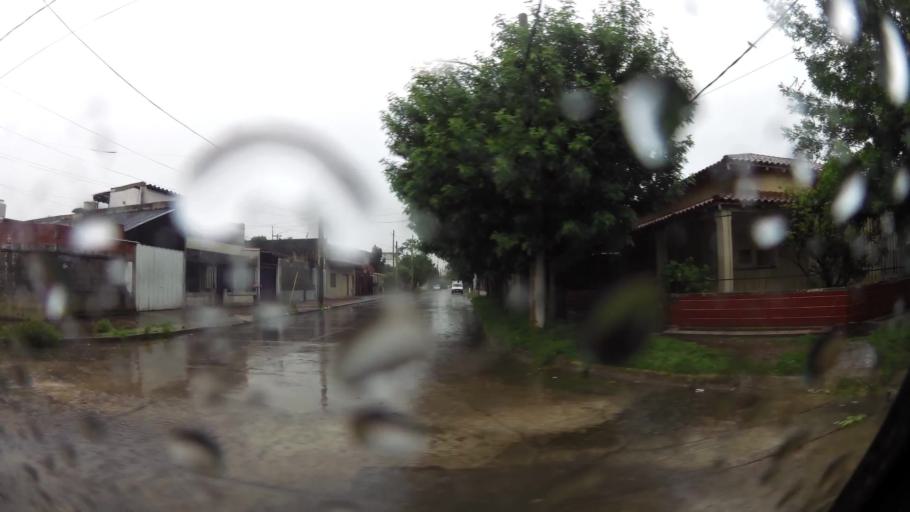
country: AR
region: Buenos Aires
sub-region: Partido de Lanus
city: Lanus
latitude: -34.7186
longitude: -58.4102
